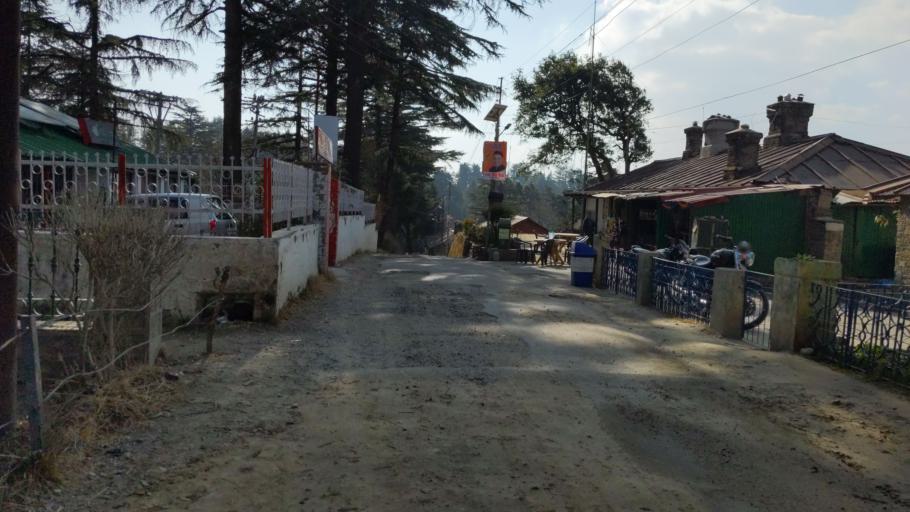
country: IN
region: Uttarakhand
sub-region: Almora
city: Almora
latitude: 29.4734
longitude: 79.6470
